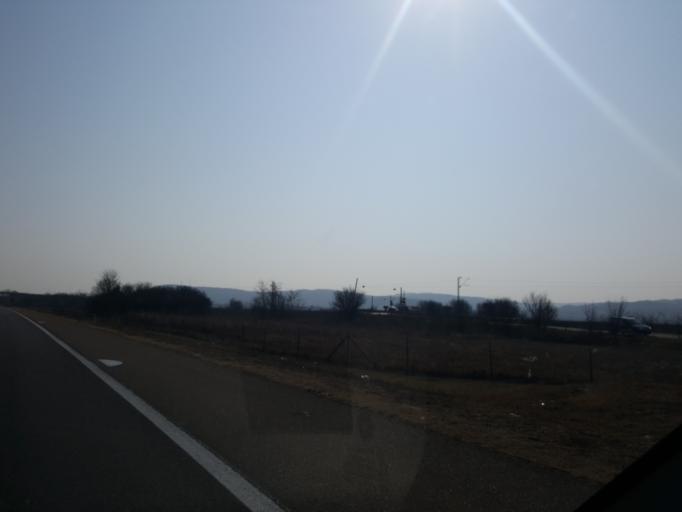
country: RS
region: Central Serbia
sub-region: Nisavski Okrug
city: Doljevac
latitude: 43.1190
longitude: 21.9163
